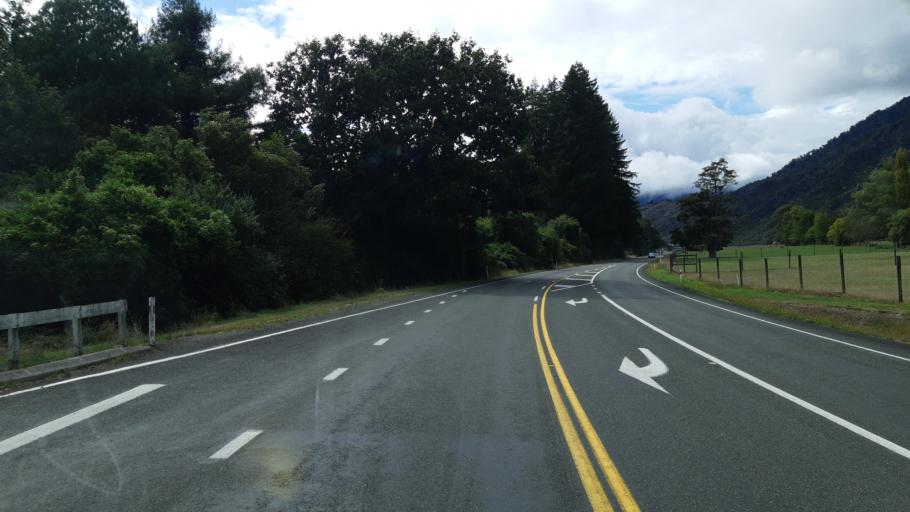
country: NZ
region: West Coast
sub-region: Buller District
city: Westport
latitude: -41.7967
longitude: 172.3397
